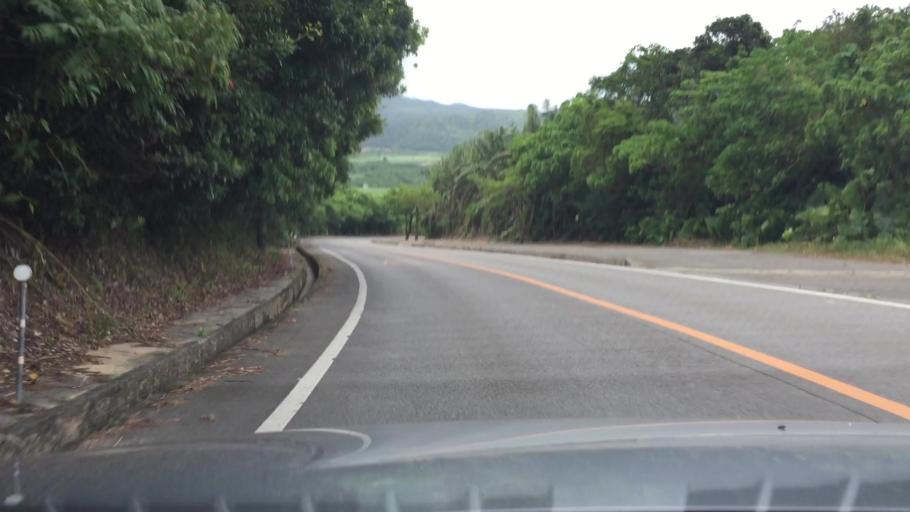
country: JP
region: Okinawa
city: Ishigaki
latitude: 24.4057
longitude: 124.2133
